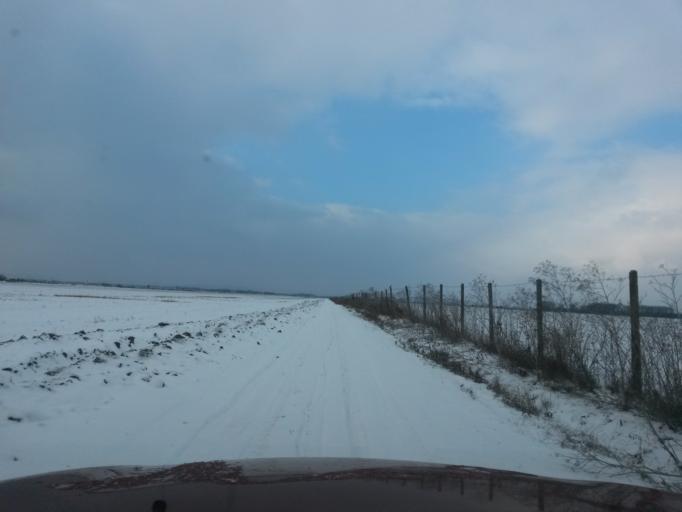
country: SK
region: Kosicky
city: Kosice
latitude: 48.6292
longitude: 21.3532
